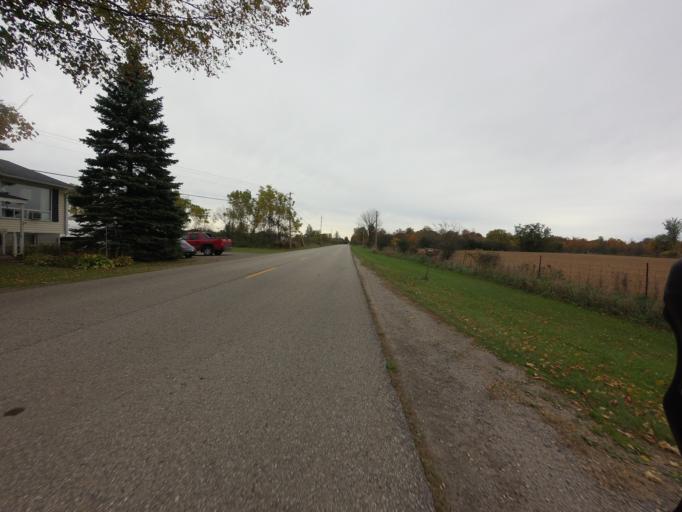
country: CA
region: Ontario
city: Brockville
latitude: 44.6821
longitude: -75.8546
